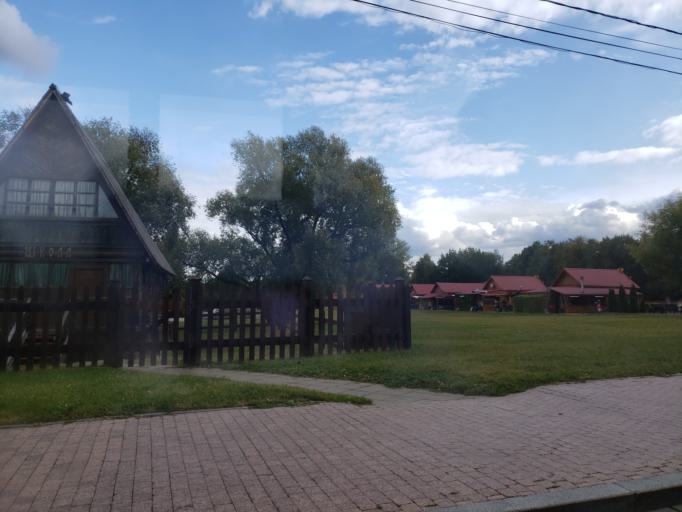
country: RU
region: Moscow
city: Kolomenskoye
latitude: 55.6718
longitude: 37.6689
